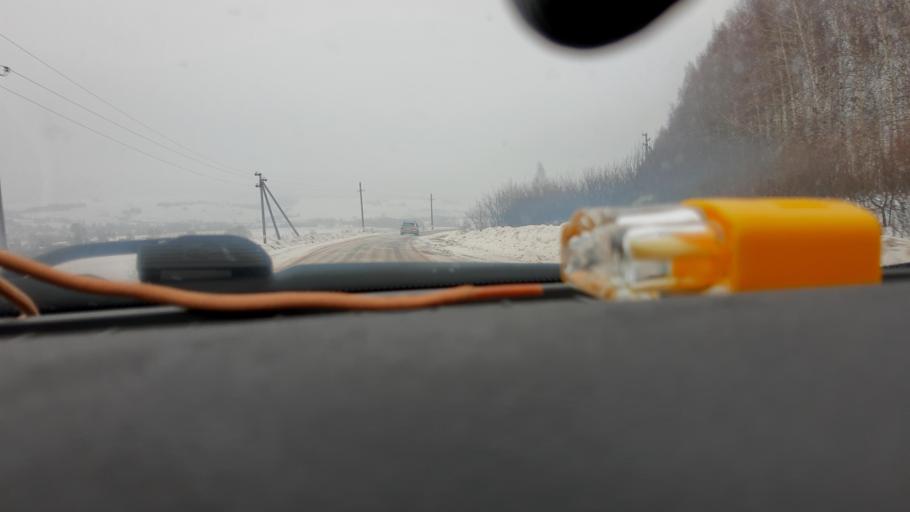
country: RU
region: Bashkortostan
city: Ulukulevo
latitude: 54.5574
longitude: 56.4353
